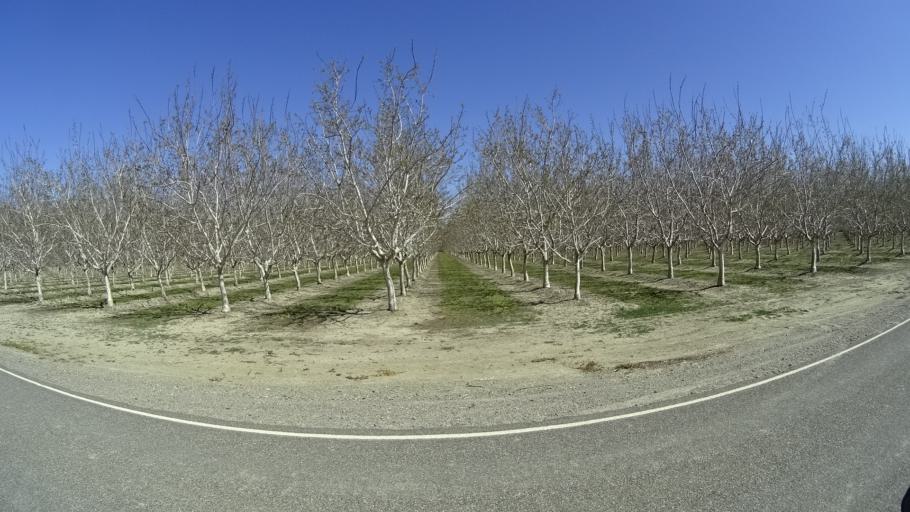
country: US
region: California
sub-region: Glenn County
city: Willows
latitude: 39.6235
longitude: -122.1076
